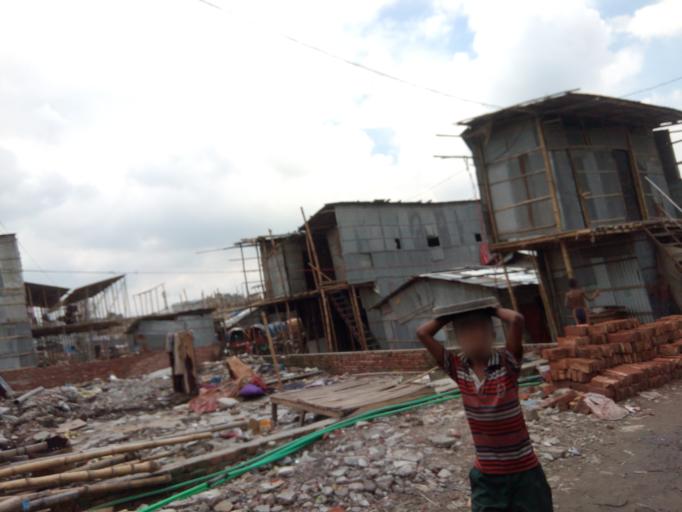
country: BD
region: Dhaka
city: Azimpur
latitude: 23.7479
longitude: 90.3611
